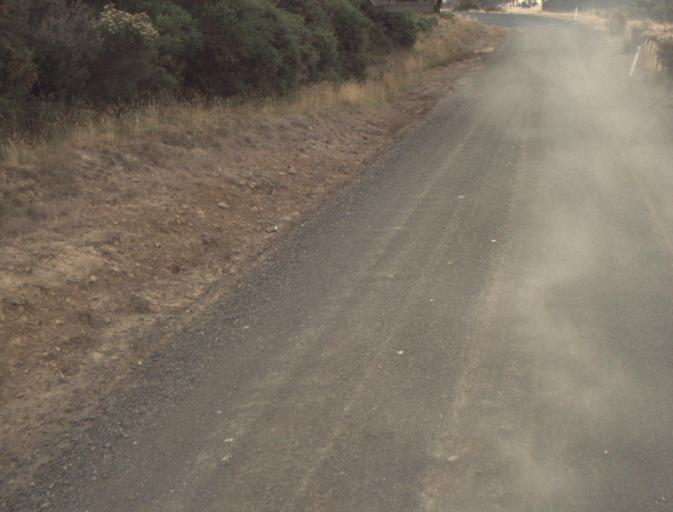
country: AU
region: Tasmania
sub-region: Northern Midlands
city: Evandale
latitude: -41.4891
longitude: 147.4373
